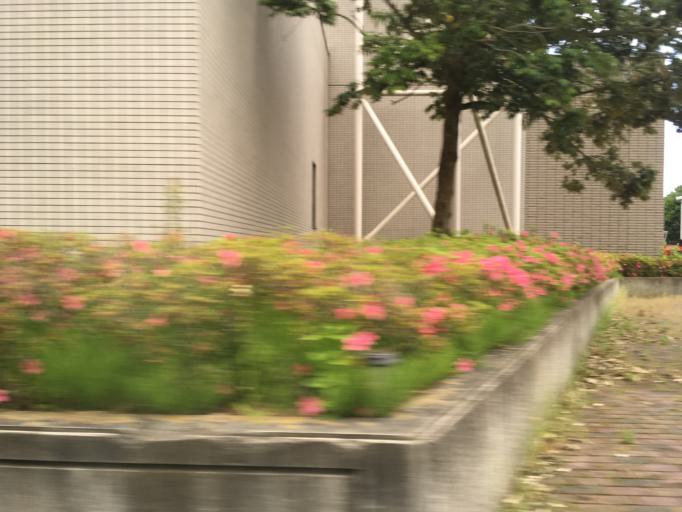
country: JP
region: Fukushima
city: Namie
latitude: 37.4947
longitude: 141.0004
